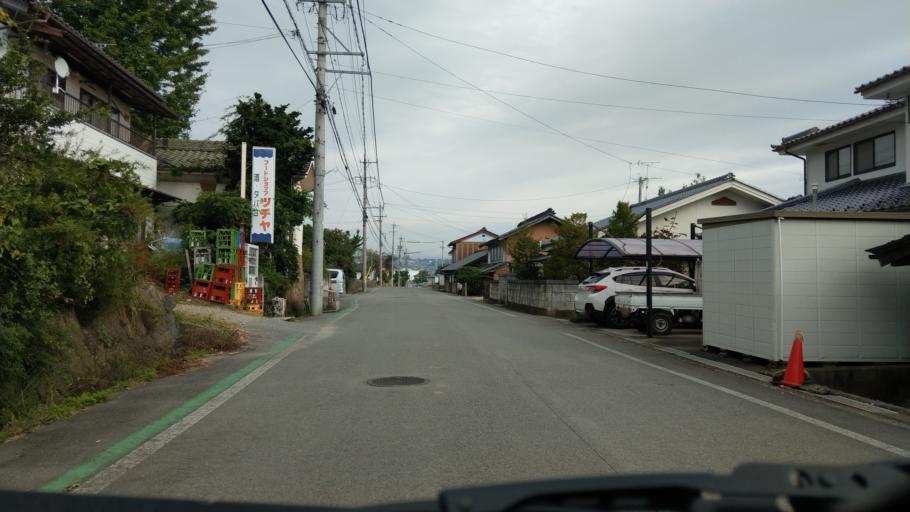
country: JP
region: Nagano
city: Komoro
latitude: 36.3391
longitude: 138.4025
